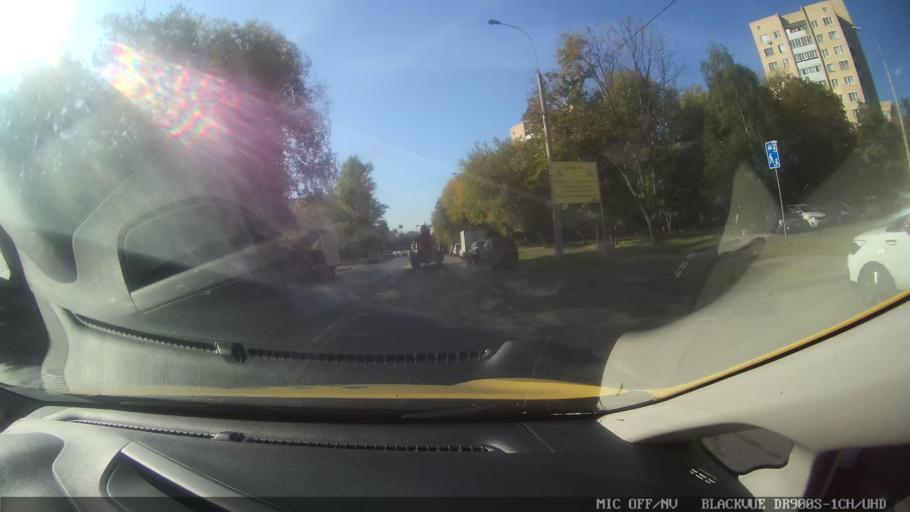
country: RU
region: Moscow
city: Kolomenskoye
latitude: 55.6785
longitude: 37.6891
